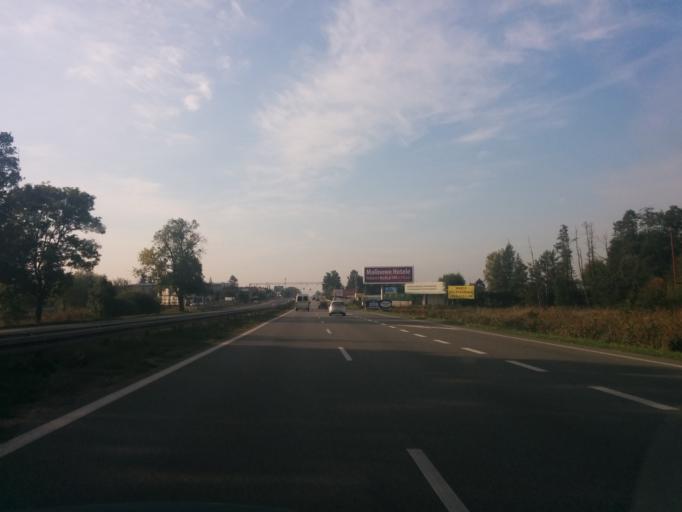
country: PL
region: Masovian Voivodeship
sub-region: Powiat piaseczynski
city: Lesznowola
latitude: 52.0856
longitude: 20.8795
